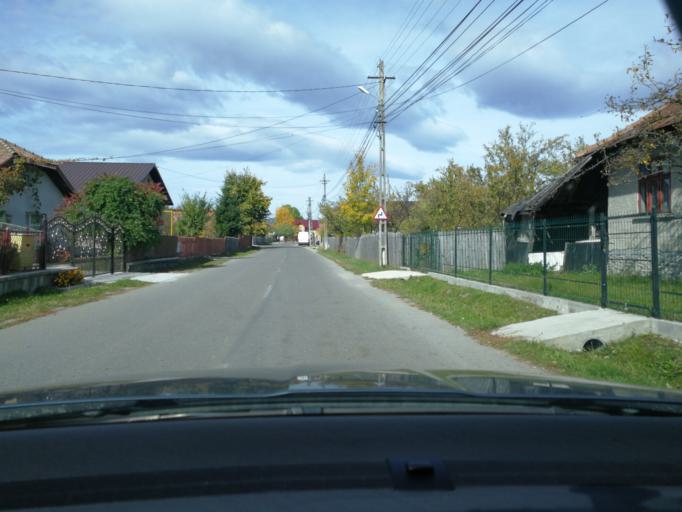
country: RO
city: Brebu Manastirei
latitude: 45.1884
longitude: 25.7653
